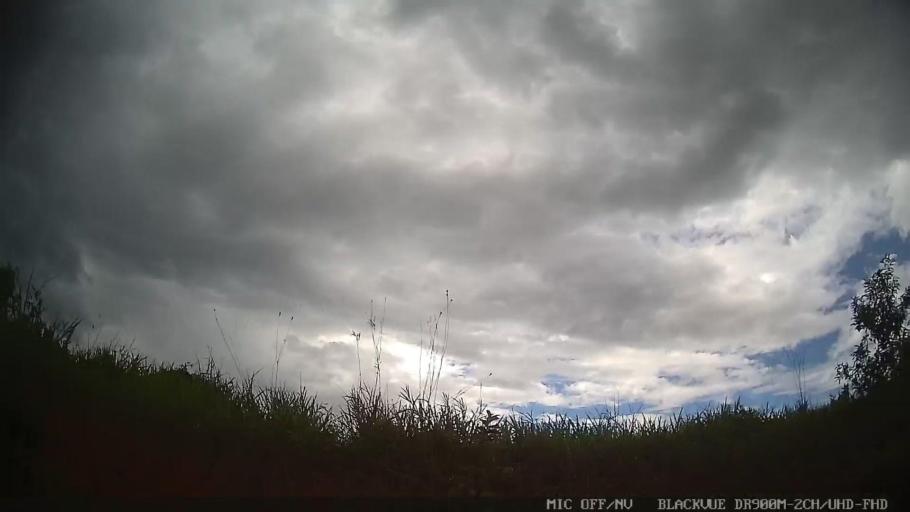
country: BR
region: Sao Paulo
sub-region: Jaguariuna
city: Jaguariuna
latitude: -22.6602
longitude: -46.9715
